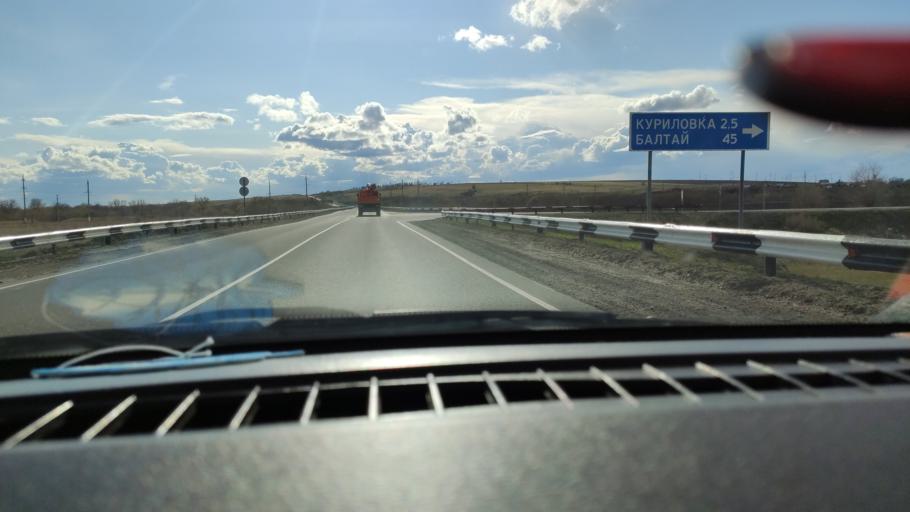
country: RU
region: Saratov
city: Sennoy
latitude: 52.1418
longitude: 46.8935
